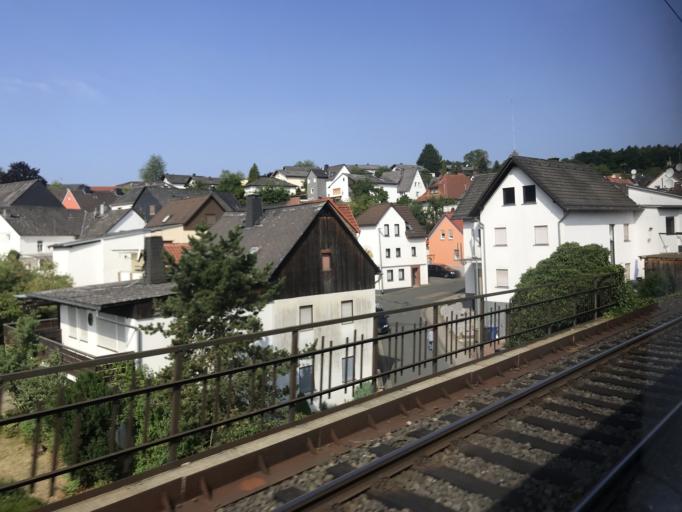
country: DE
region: Hesse
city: Bad Camberg
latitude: 50.3213
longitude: 8.2434
